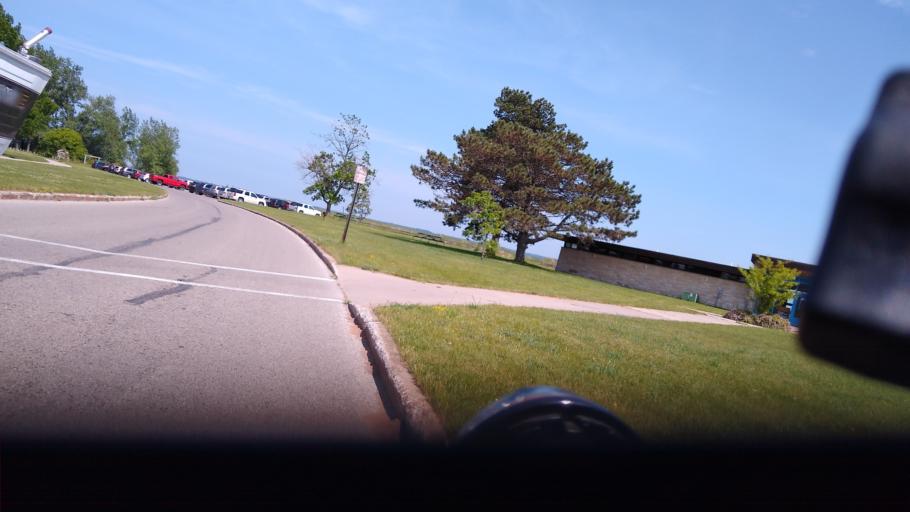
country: US
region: Michigan
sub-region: Delta County
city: Escanaba
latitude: 45.7393
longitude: -87.0475
